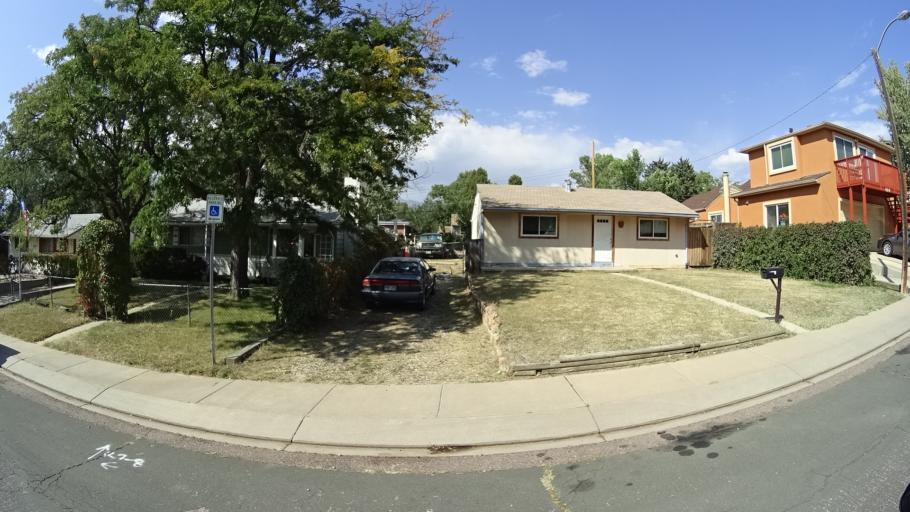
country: US
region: Colorado
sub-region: El Paso County
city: Colorado Springs
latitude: 38.8225
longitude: -104.7915
